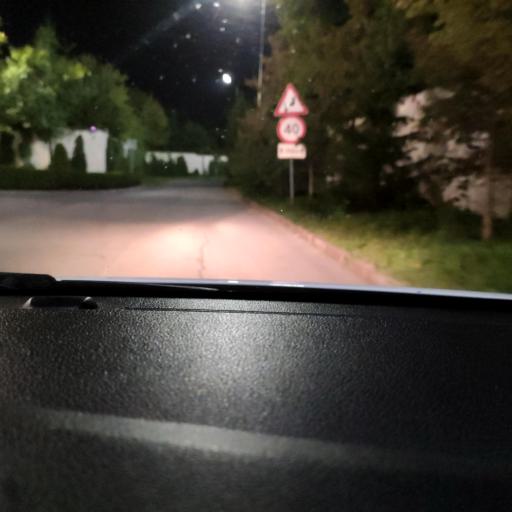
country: RU
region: Tatarstan
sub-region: Gorod Kazan'
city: Kazan
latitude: 55.7425
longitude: 49.1659
